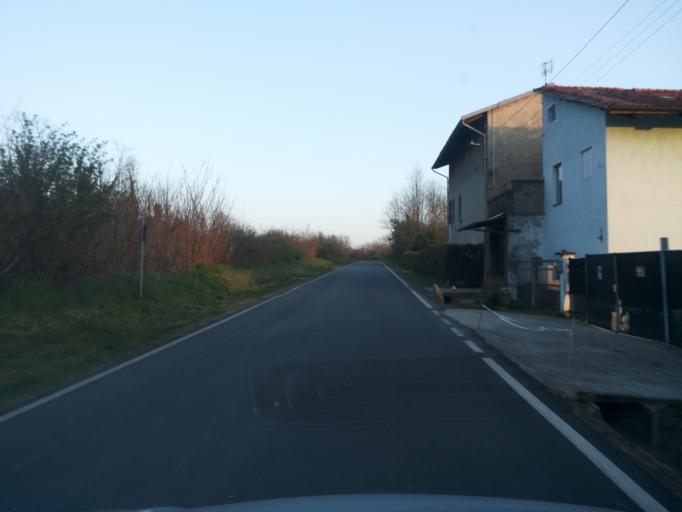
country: IT
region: Piedmont
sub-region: Provincia di Torino
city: Vestigne
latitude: 45.3826
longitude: 7.9631
